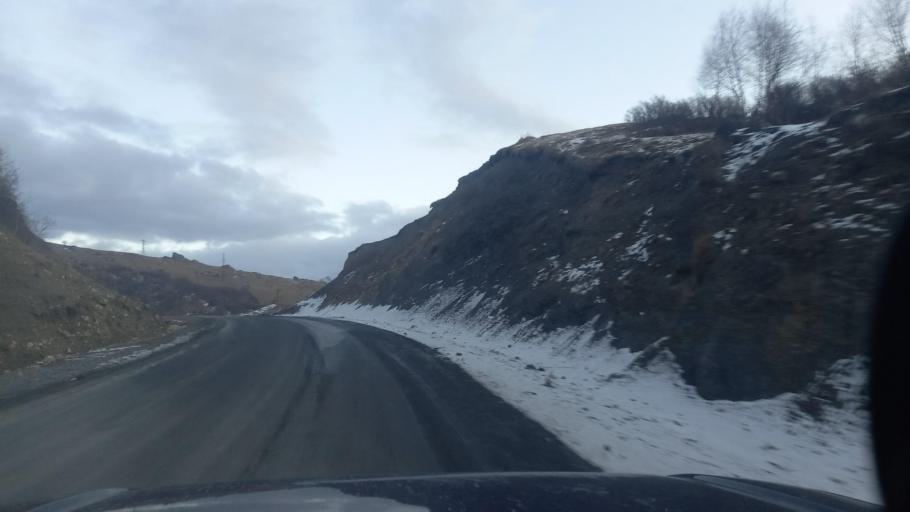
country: RU
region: Ingushetiya
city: Dzhayrakh
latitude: 42.8217
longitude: 44.8208
